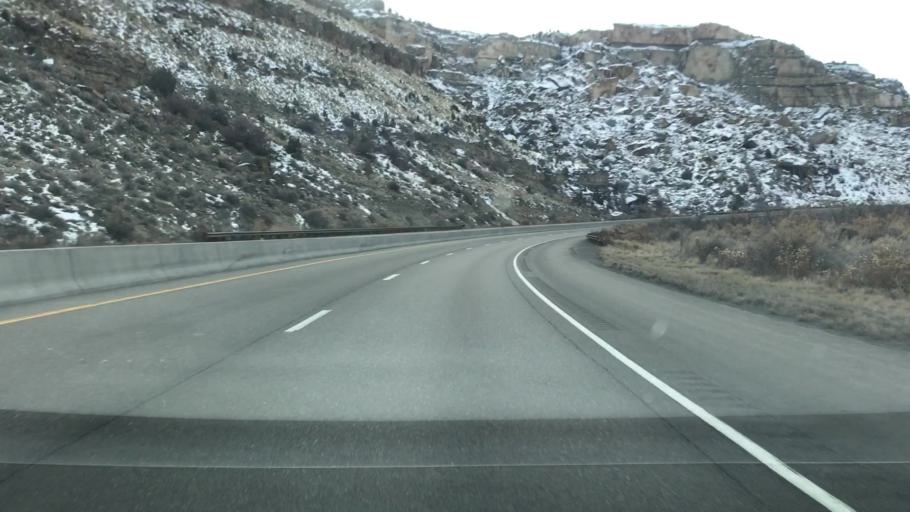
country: US
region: Colorado
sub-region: Mesa County
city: Palisade
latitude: 39.2111
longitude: -108.2565
